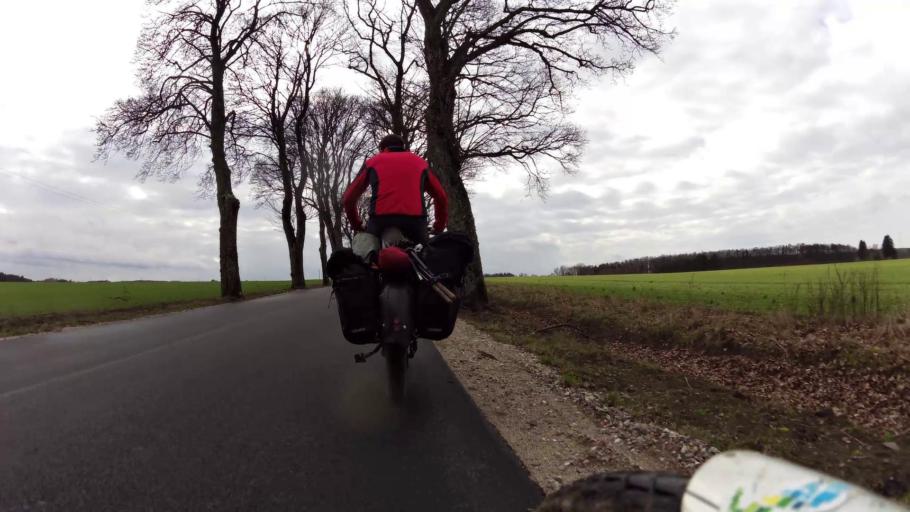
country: PL
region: Pomeranian Voivodeship
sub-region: Powiat bytowski
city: Kolczyglowy
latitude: 54.2351
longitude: 17.2425
